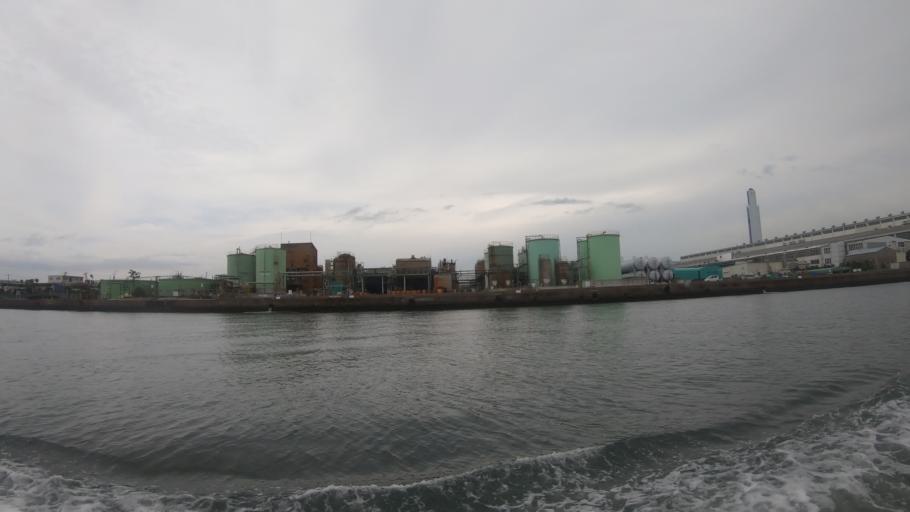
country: JP
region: Kanagawa
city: Yokohama
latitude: 35.4816
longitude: 139.6820
